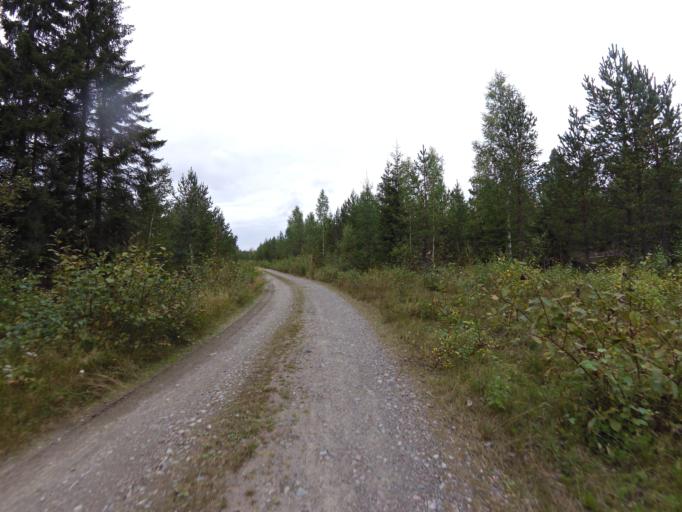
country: SE
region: Gaevleborg
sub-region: Gavle Kommun
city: Valbo
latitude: 60.7482
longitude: 16.9821
